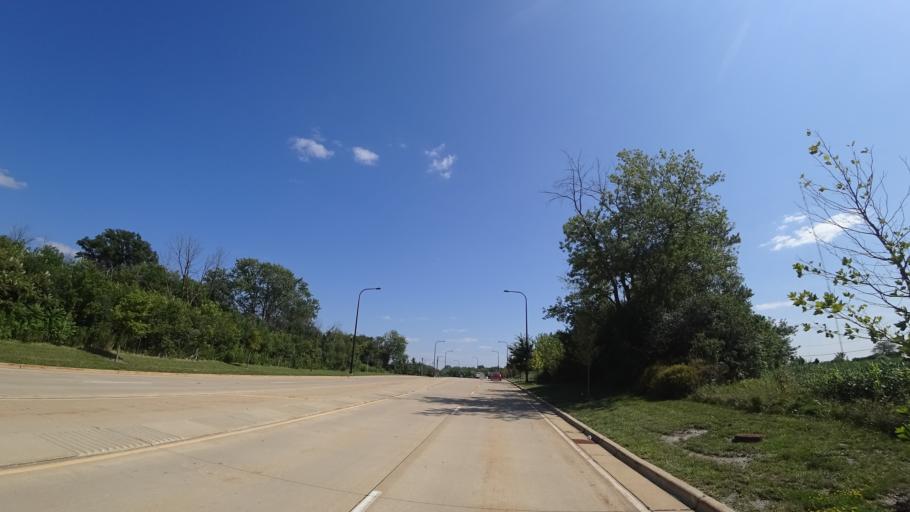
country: US
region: Illinois
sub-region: Cook County
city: Orland Hills
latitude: 41.5596
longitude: -87.8481
